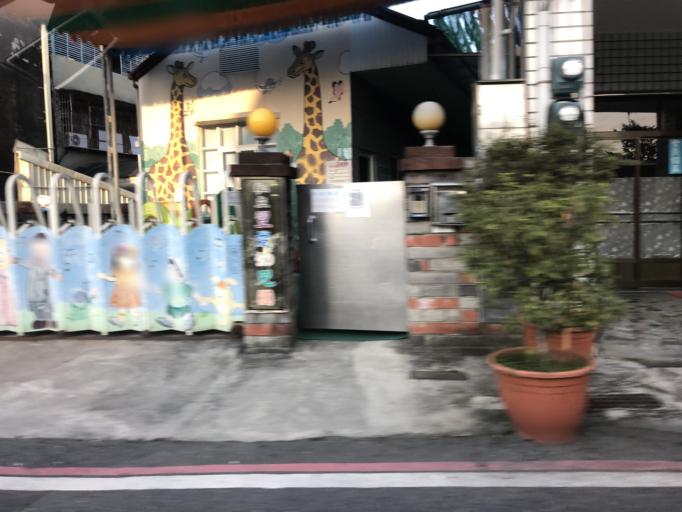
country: TW
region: Taiwan
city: Xinying
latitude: 23.1783
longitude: 120.2526
